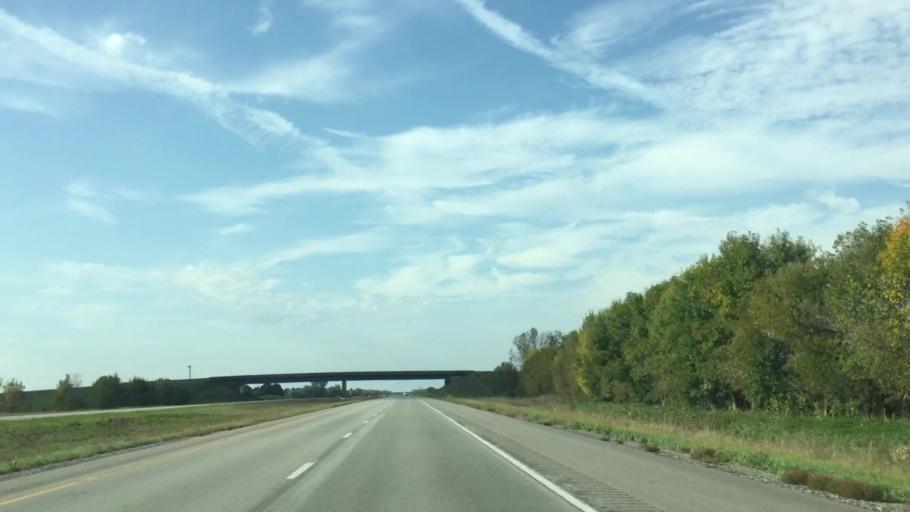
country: US
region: Illinois
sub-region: Rock Island County
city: Port Byron
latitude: 41.5853
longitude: -90.2048
